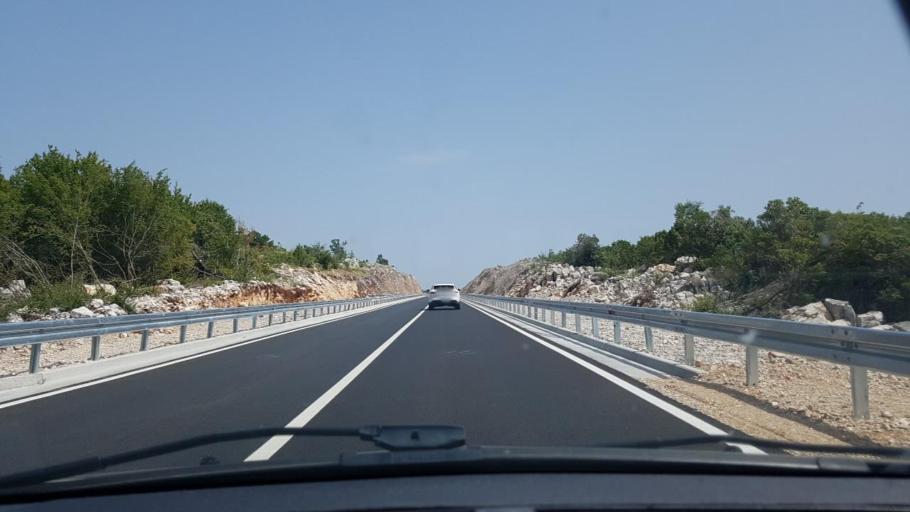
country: HR
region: Dubrovacko-Neretvanska
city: Podgora
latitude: 42.9476
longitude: 17.7628
